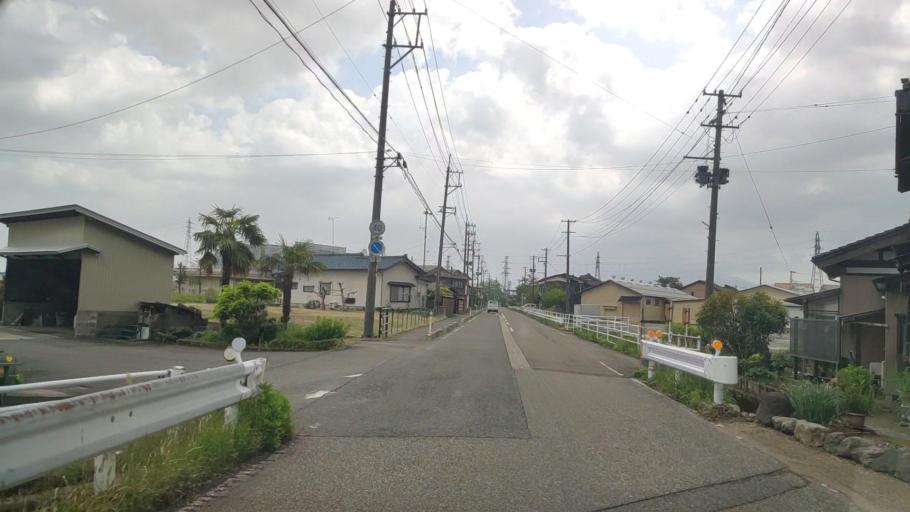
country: JP
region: Niigata
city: Gosen
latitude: 37.7356
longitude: 139.1680
